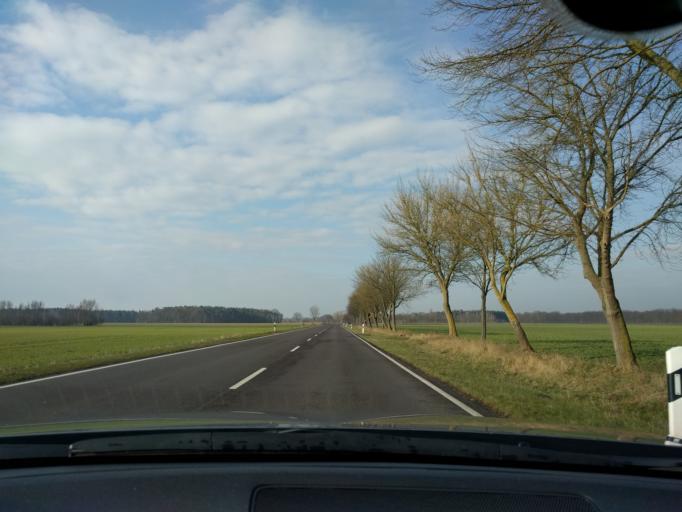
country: DE
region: Saxony-Anhalt
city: Hassel
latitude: 52.6594
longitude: 11.9309
